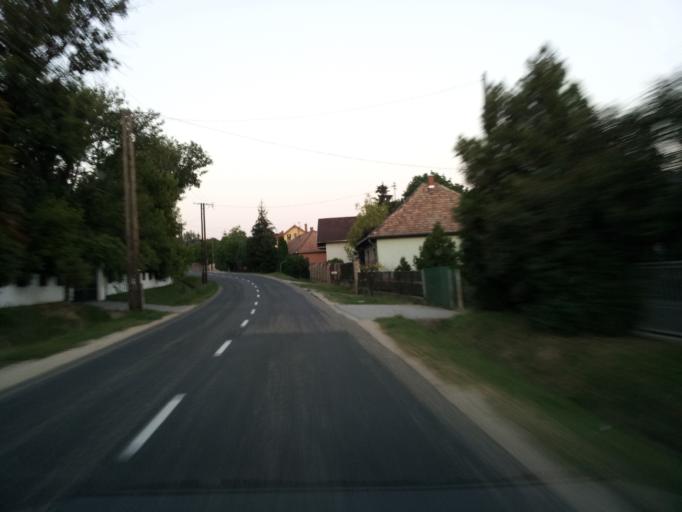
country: HU
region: Fejer
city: Bicske
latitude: 47.4910
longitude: 18.5706
